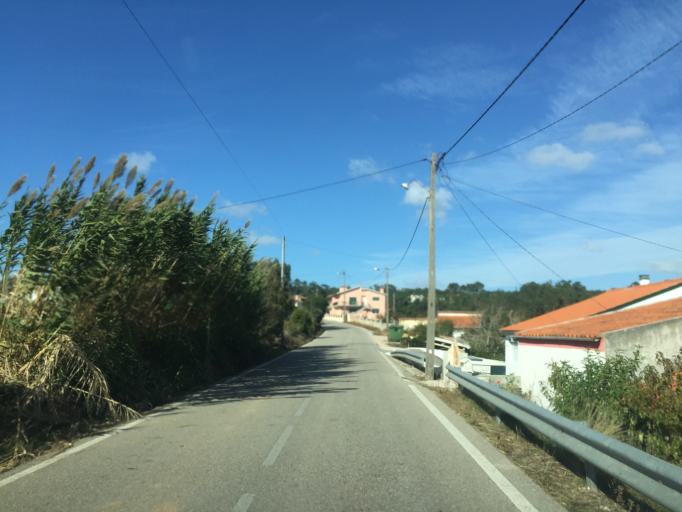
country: PT
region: Coimbra
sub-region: Figueira da Foz
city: Tavarede
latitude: 40.1810
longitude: -8.8376
